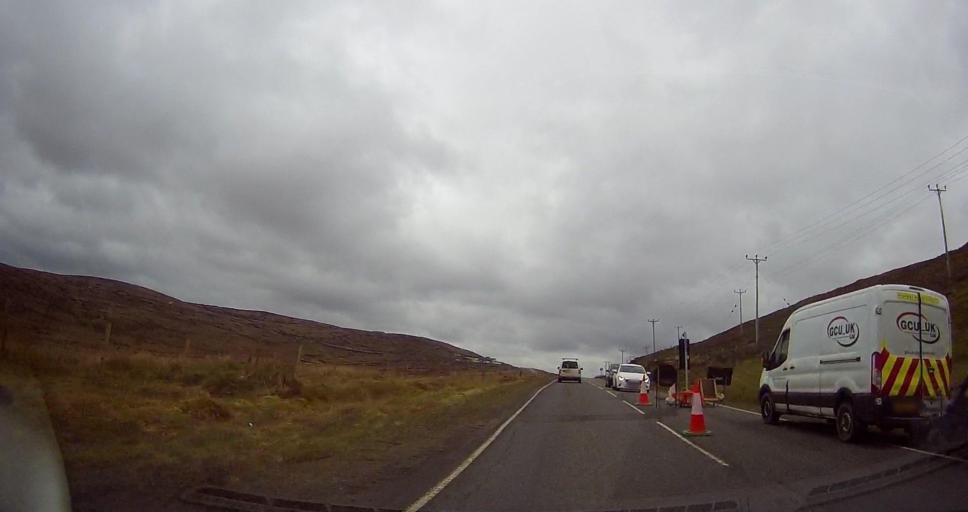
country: GB
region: Scotland
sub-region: Shetland Islands
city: Lerwick
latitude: 60.3338
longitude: -1.2541
